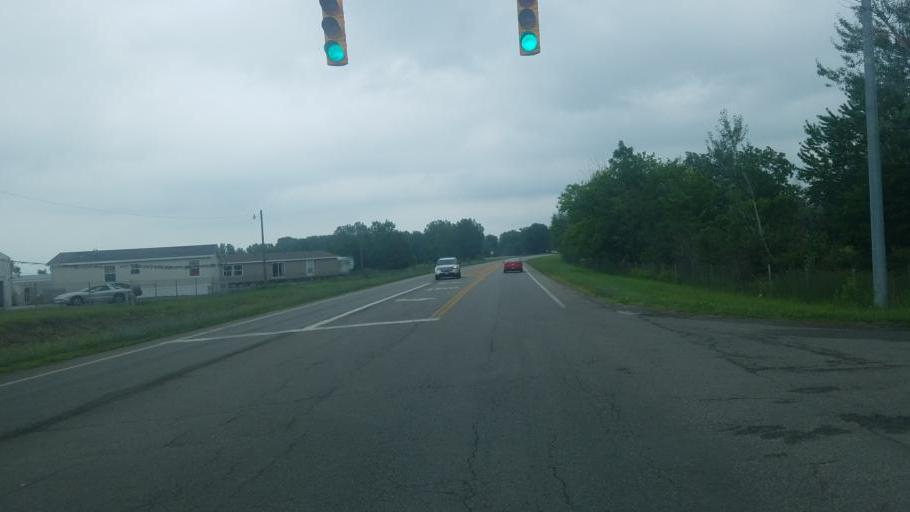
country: US
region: Ohio
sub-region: Logan County
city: Lakeview
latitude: 40.4793
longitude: -83.9080
